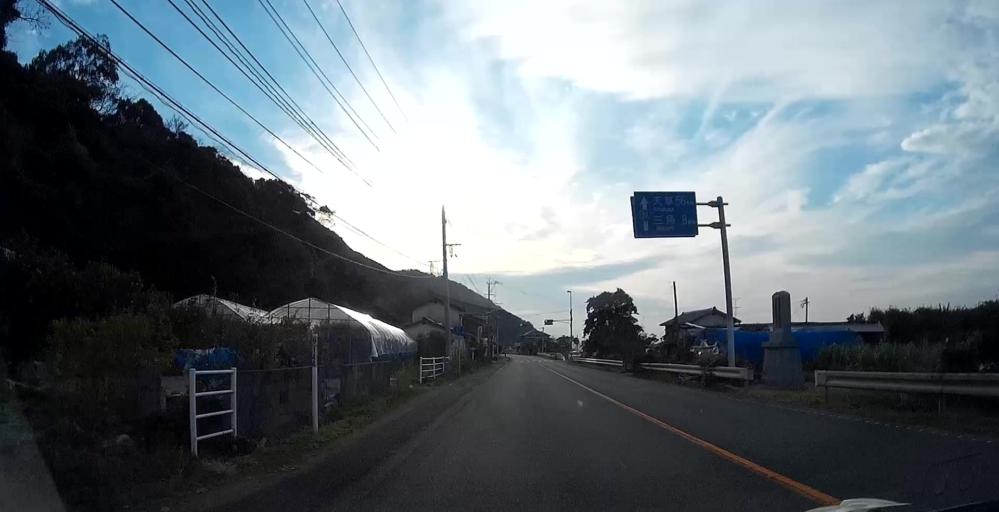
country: JP
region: Kumamoto
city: Matsubase
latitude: 32.6490
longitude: 130.4934
